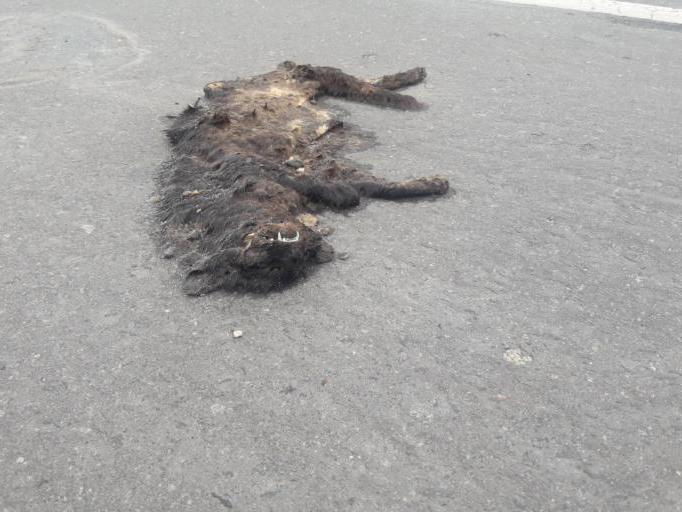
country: AR
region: Entre Rios
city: Parana
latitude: -31.6739
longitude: -60.5767
